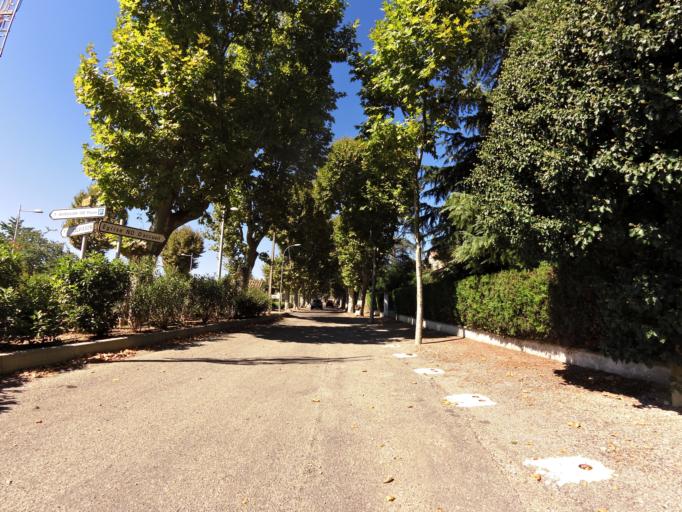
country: FR
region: Languedoc-Roussillon
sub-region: Departement du Gard
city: Codognan
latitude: 43.7358
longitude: 4.2197
